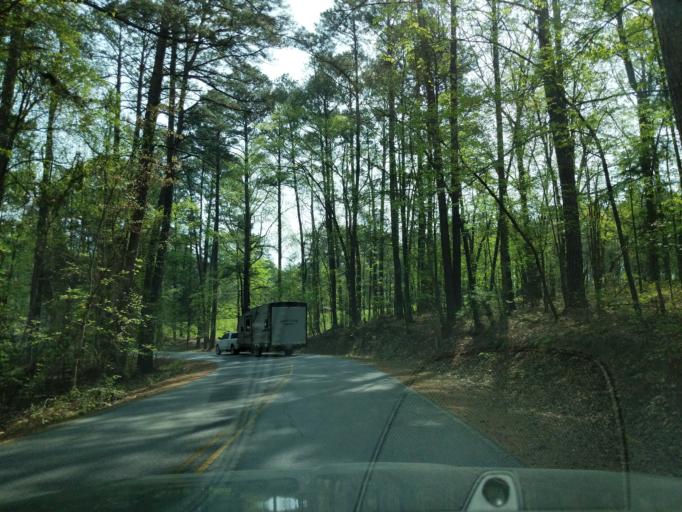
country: US
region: Georgia
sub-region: Lincoln County
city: Lincolnton
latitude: 33.8496
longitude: -82.3992
